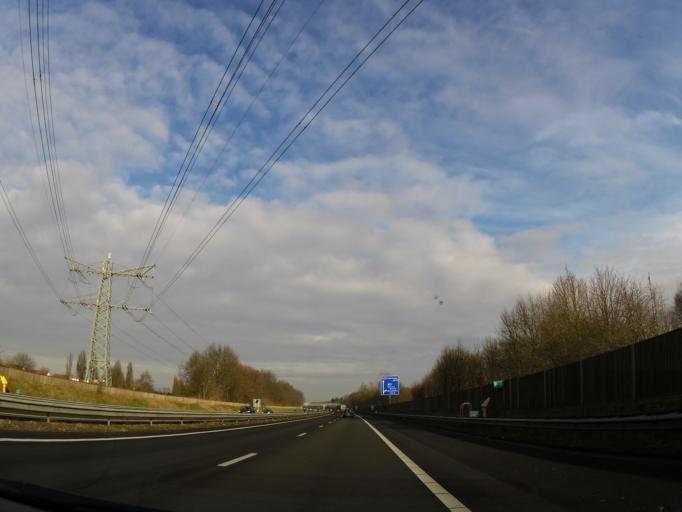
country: NL
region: Limburg
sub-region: Gemeente Venray
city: Venray
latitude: 51.5333
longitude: 5.9999
